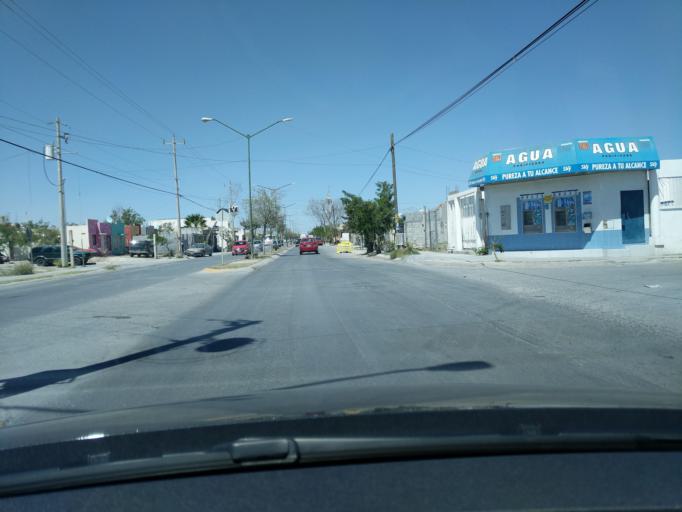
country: MX
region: Nuevo Leon
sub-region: Pesqueria
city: Colinas del Aeropuerto
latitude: 25.8235
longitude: -100.1115
